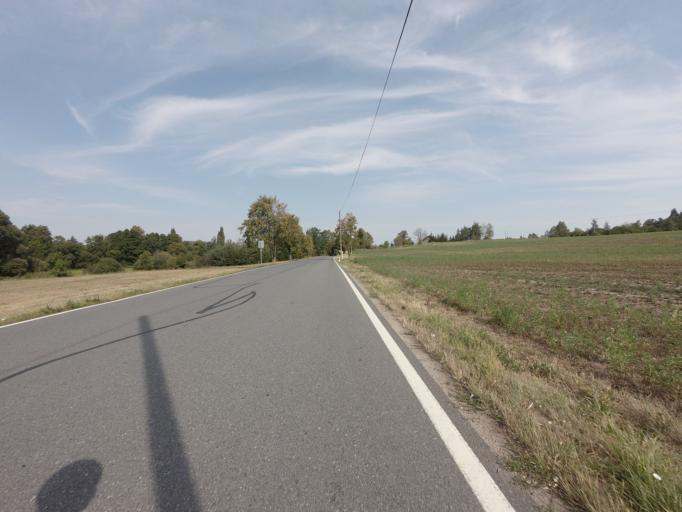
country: CZ
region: Central Bohemia
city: Petrovice
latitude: 49.5480
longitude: 14.3451
